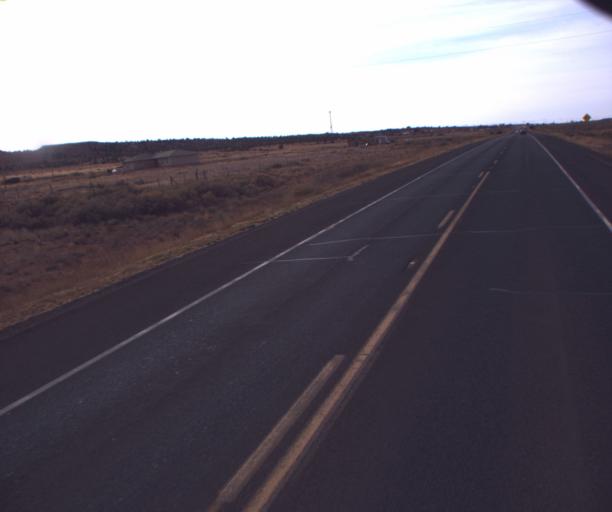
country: US
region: Arizona
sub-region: Apache County
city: Ganado
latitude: 35.7659
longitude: -109.6238
